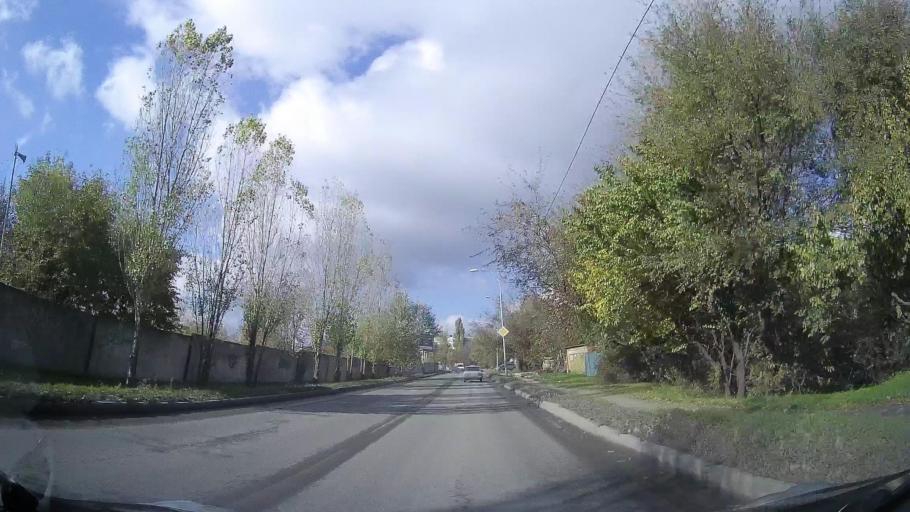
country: RU
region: Rostov
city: Rostov-na-Donu
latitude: 47.2253
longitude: 39.6833
